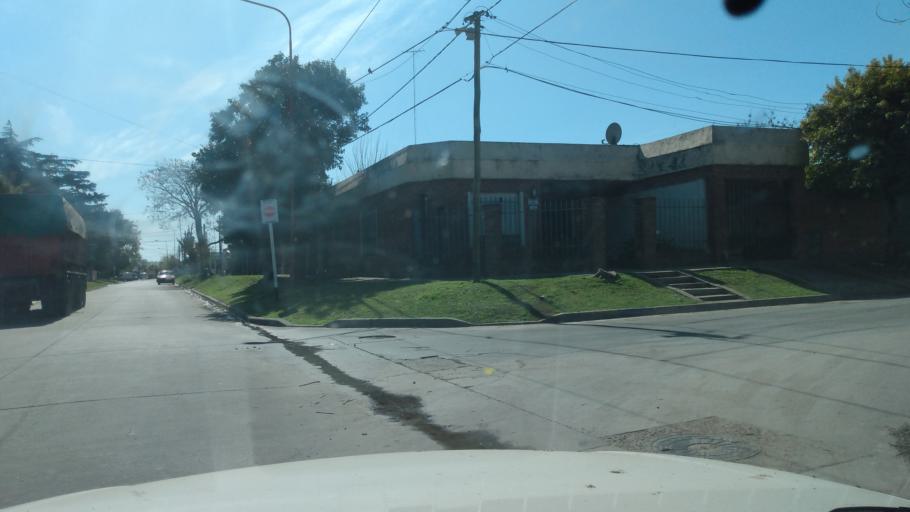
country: AR
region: Buenos Aires
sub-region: Partido de Lujan
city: Lujan
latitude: -34.5841
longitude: -59.1083
